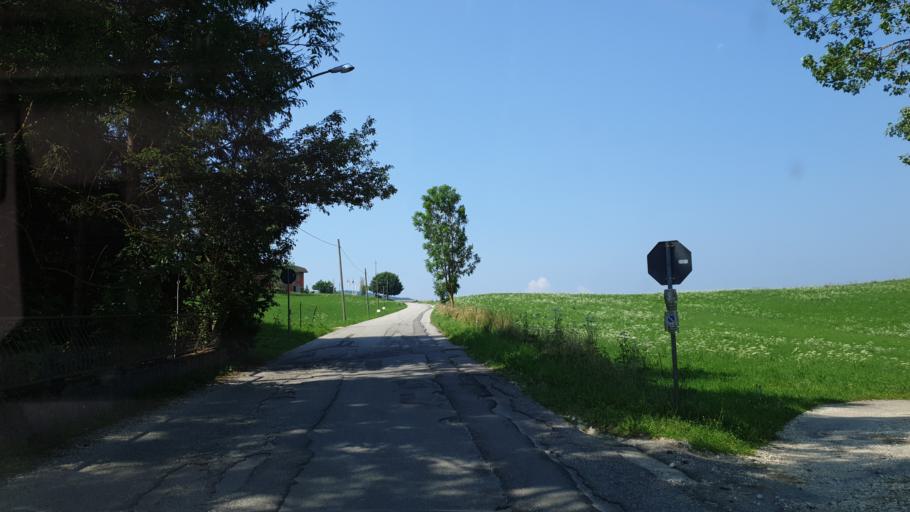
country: IT
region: Veneto
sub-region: Provincia di Vicenza
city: Canove di Roana
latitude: 45.8549
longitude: 11.4972
